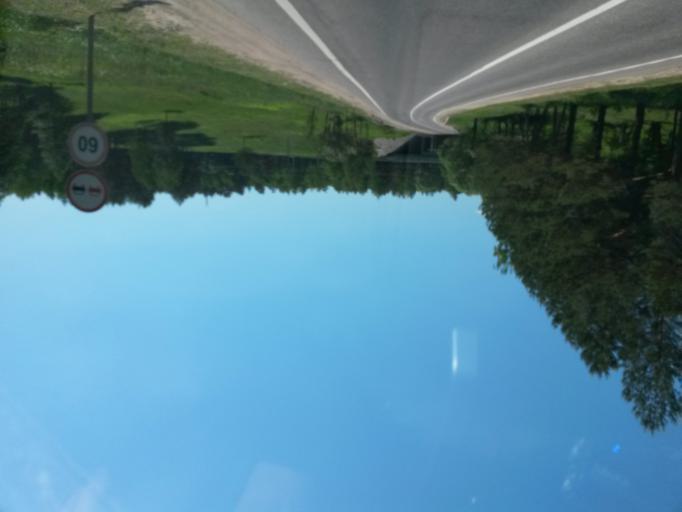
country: RU
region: Moskovskaya
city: Danki
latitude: 54.9066
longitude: 37.5090
